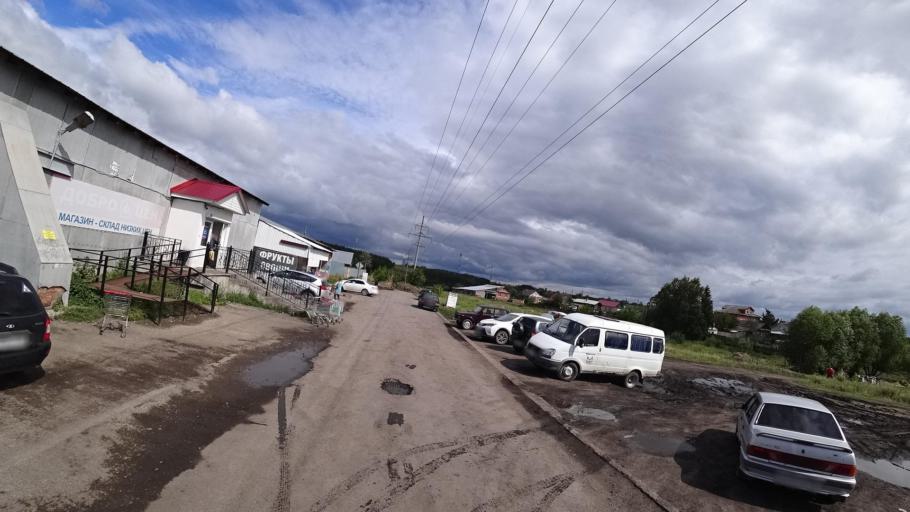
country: RU
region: Sverdlovsk
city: Kamyshlov
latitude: 56.8639
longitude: 62.7107
